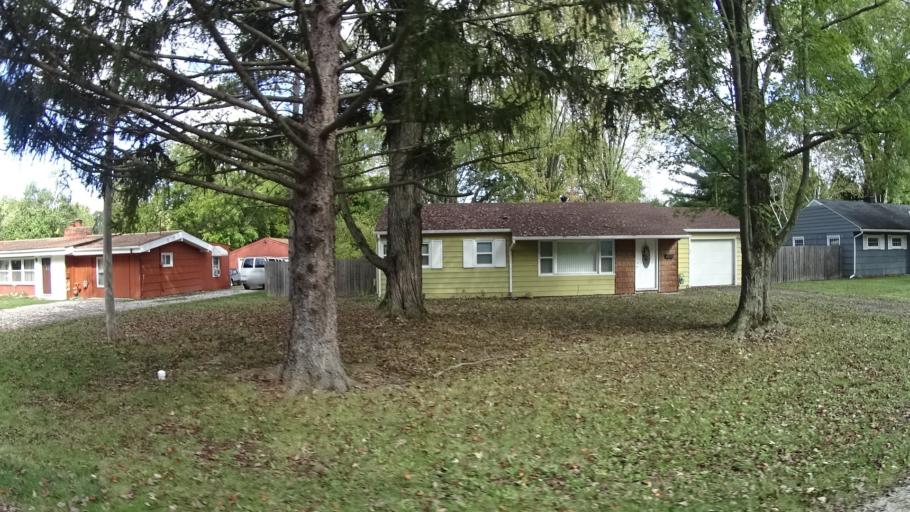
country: US
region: Ohio
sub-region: Lorain County
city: Grafton
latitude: 41.3149
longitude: -82.0759
